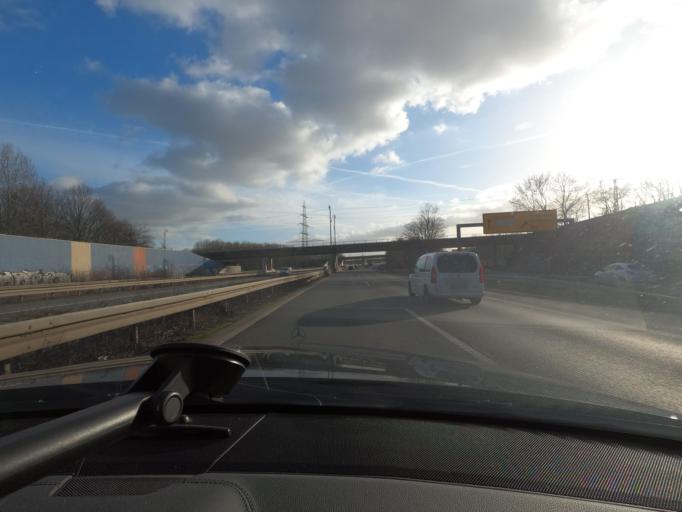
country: DE
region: North Rhine-Westphalia
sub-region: Regierungsbezirk Arnsberg
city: Dortmund
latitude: 51.5380
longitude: 7.5173
